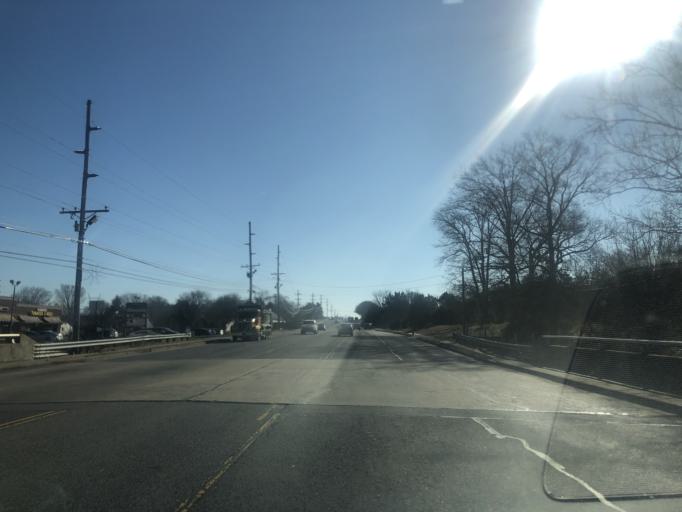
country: US
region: Tennessee
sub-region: Rutherford County
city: Smyrna
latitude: 35.9815
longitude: -86.5437
